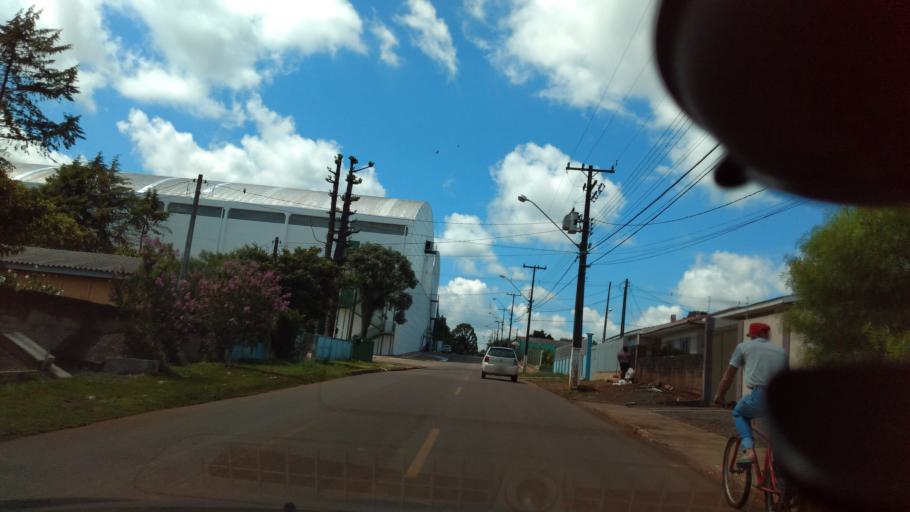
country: BR
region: Parana
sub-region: Guarapuava
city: Guarapuava
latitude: -25.3964
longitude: -51.4987
